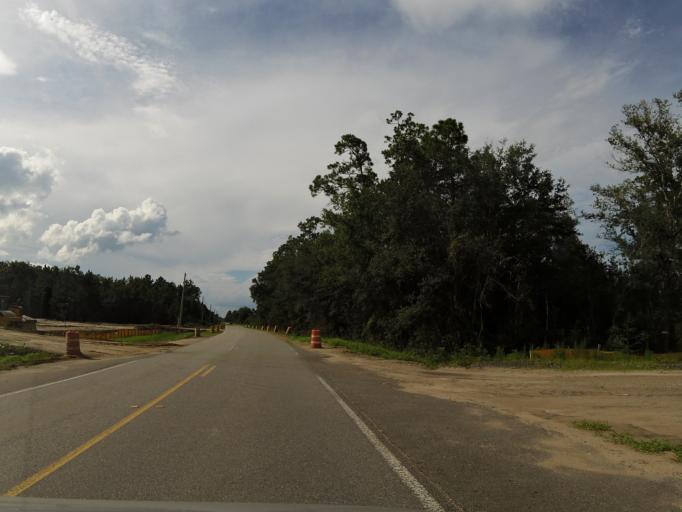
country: US
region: Florida
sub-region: Clay County
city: Green Cove Springs
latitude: 29.9542
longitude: -81.6662
